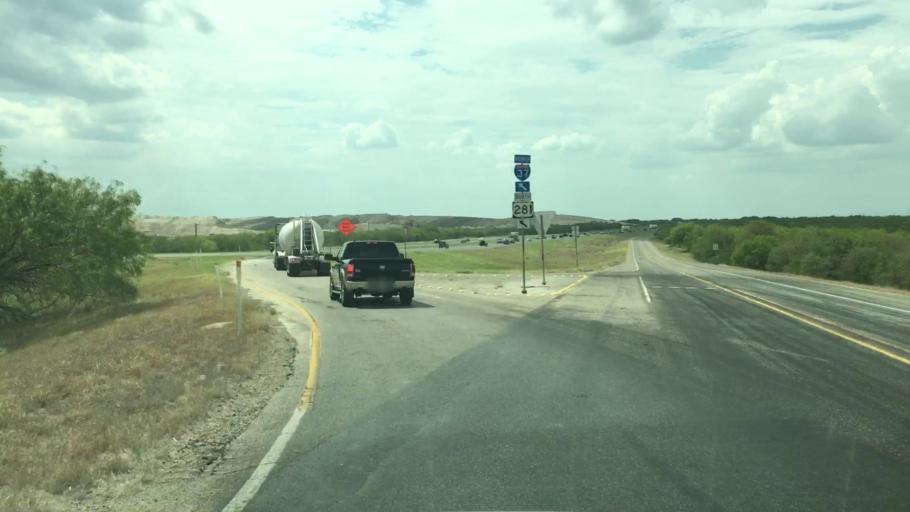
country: US
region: Texas
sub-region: Atascosa County
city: Pleasanton
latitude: 28.7866
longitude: -98.3230
